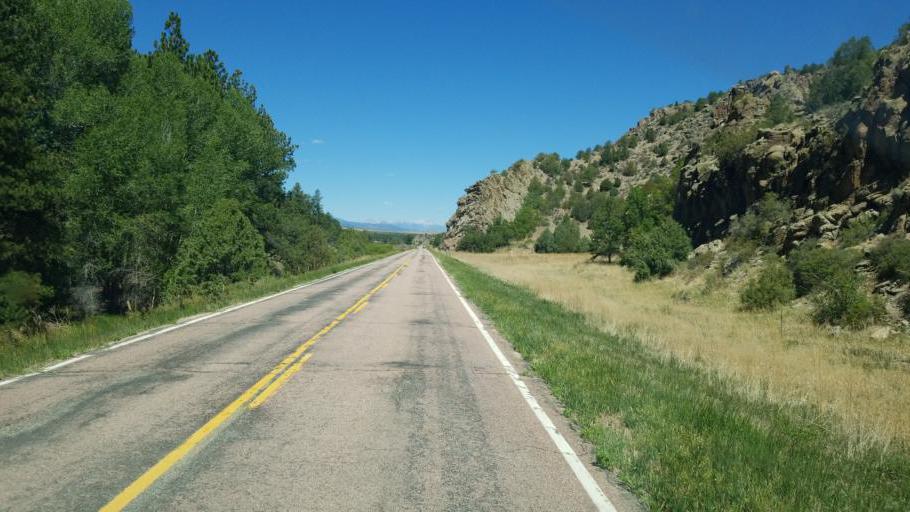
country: US
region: Colorado
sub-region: Custer County
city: Westcliffe
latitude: 38.2524
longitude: -105.5829
